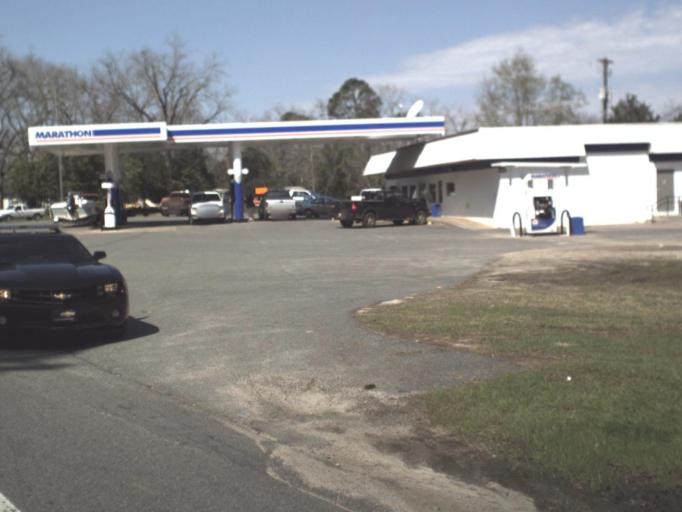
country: US
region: Florida
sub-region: Gadsden County
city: Havana
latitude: 30.6200
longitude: -84.4265
